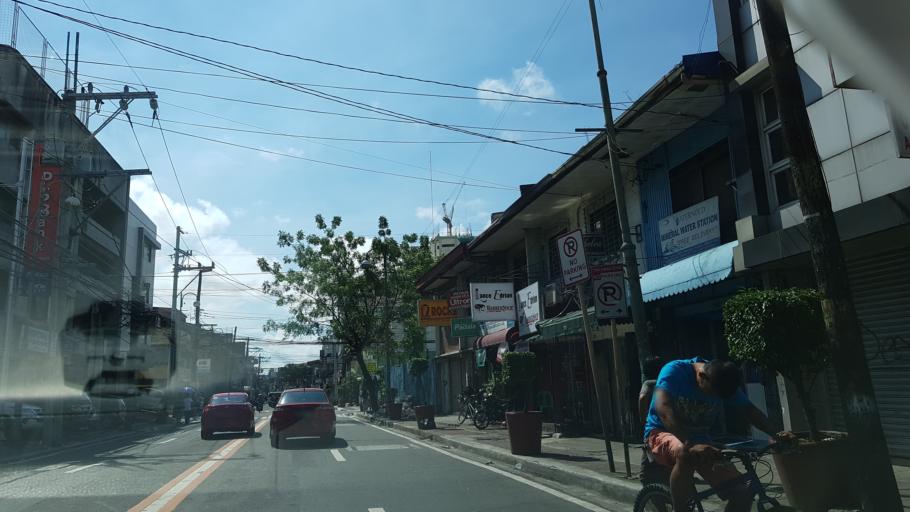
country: PH
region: Metro Manila
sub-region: Mandaluyong
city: Mandaluyong City
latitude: 14.5704
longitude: 121.0221
